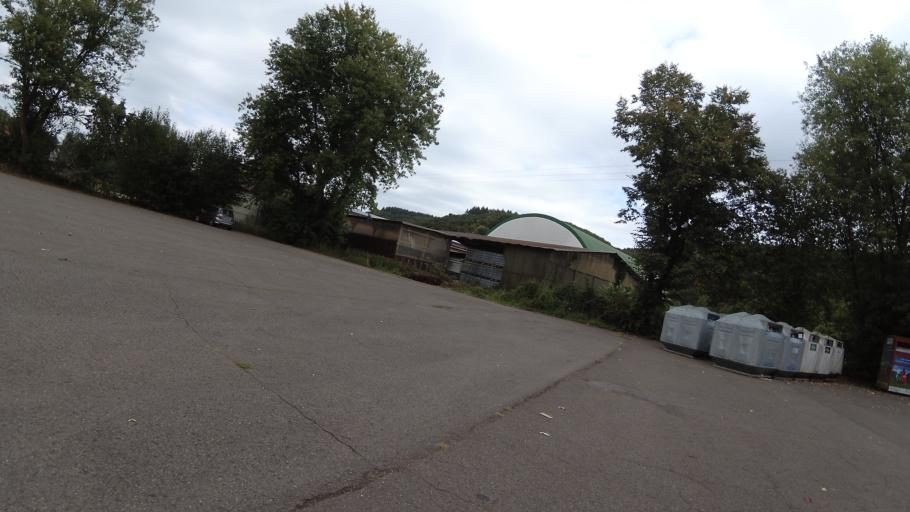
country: DE
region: Saarland
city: Wadern
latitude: 49.5048
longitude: 6.8704
